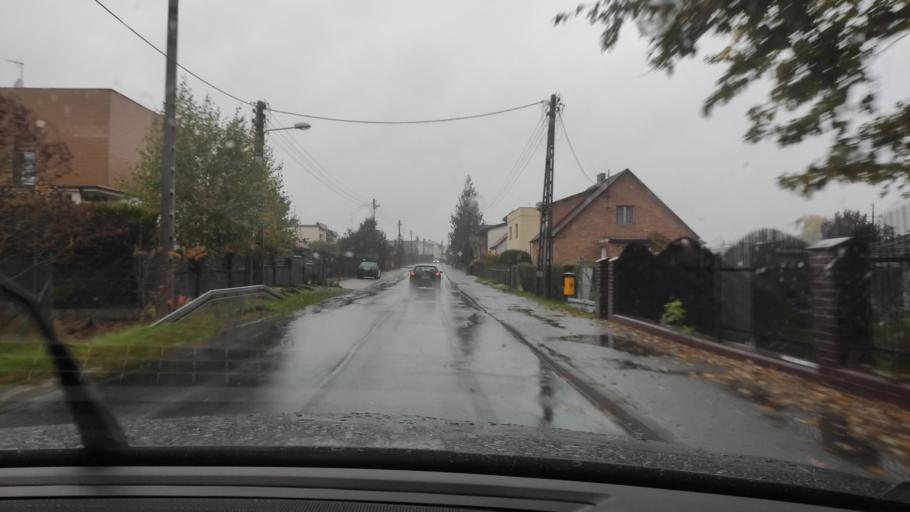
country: PL
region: Greater Poland Voivodeship
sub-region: Powiat poznanski
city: Kornik
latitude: 52.2219
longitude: 17.0973
